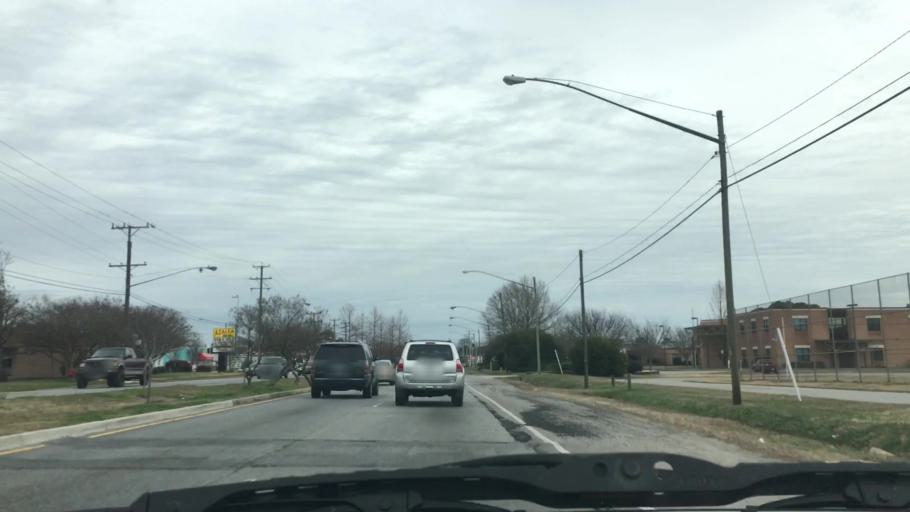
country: US
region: Virginia
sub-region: City of Norfolk
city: Norfolk
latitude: 36.9151
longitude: -76.2191
